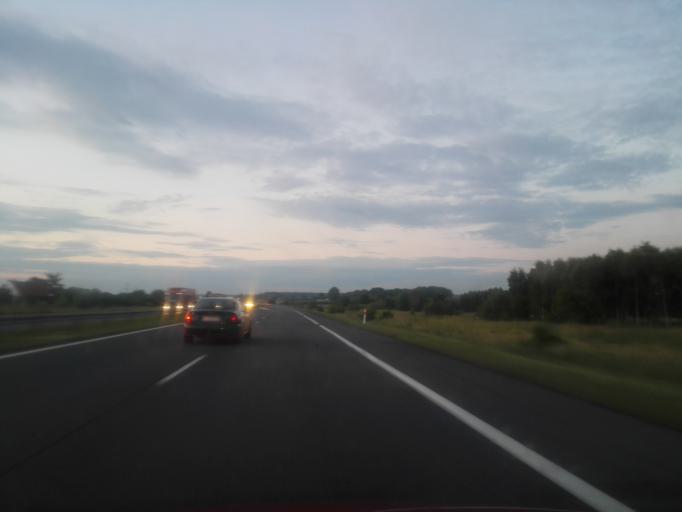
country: PL
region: Lodz Voivodeship
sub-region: Powiat piotrkowski
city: Wola Krzysztoporska
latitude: 51.3098
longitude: 19.5667
